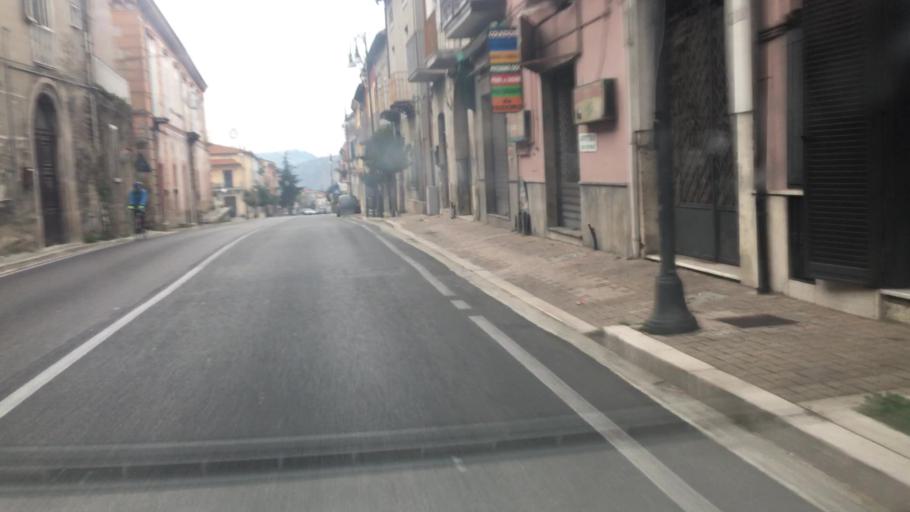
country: IT
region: Campania
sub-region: Provincia di Benevento
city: Arpaia
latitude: 41.0372
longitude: 14.5499
